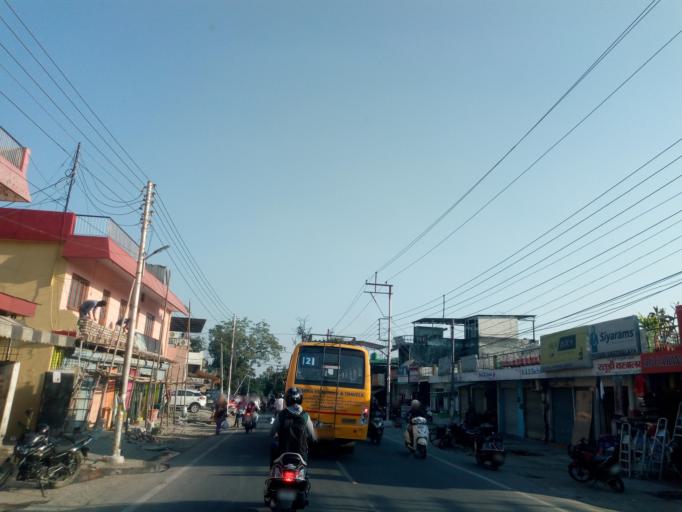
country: IN
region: Uttarakhand
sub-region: Dehradun
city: Dehradun
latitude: 30.3411
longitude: 78.0504
